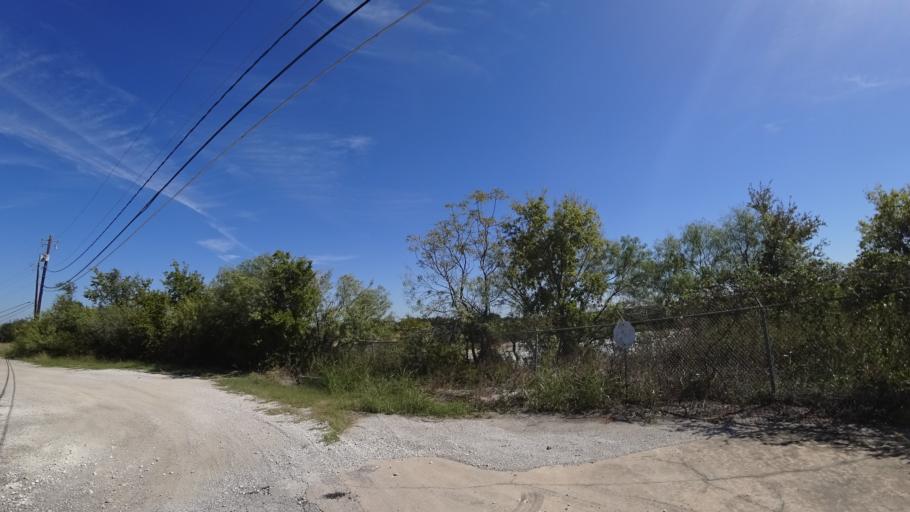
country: US
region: Texas
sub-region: Travis County
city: Austin
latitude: 30.1850
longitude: -97.7065
